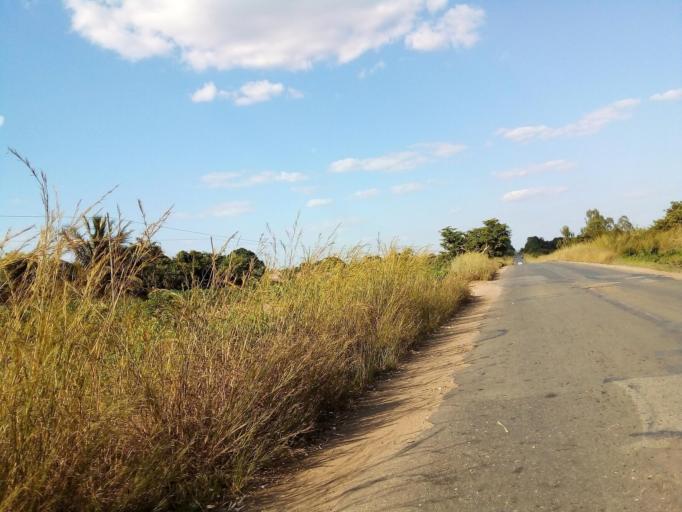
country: MZ
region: Zambezia
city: Quelimane
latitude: -17.5747
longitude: 36.6178
